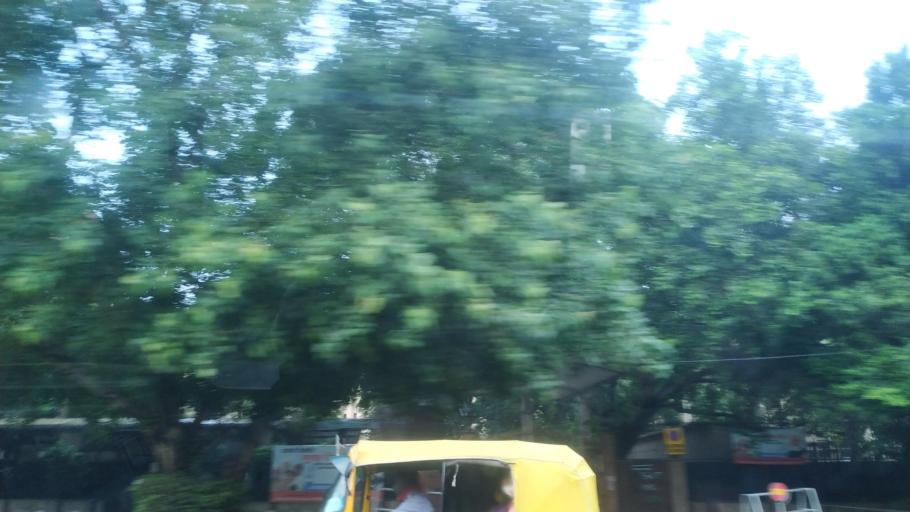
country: IN
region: NCT
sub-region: New Delhi
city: New Delhi
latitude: 28.6206
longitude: 77.2126
